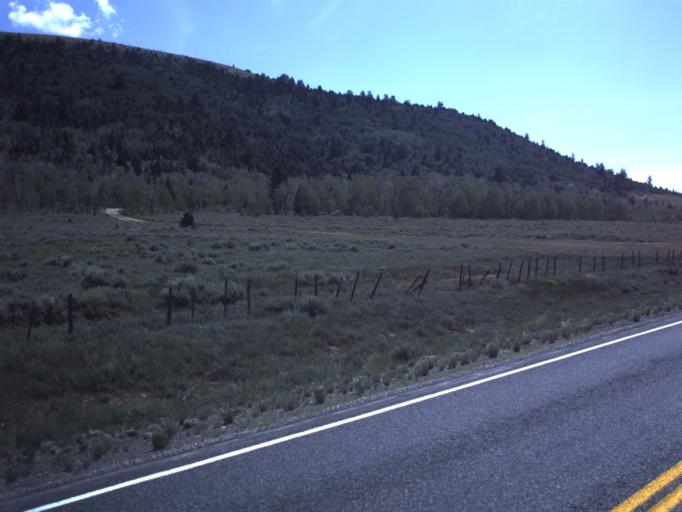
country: US
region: Utah
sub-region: Carbon County
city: Helper
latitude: 39.8633
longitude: -111.1140
